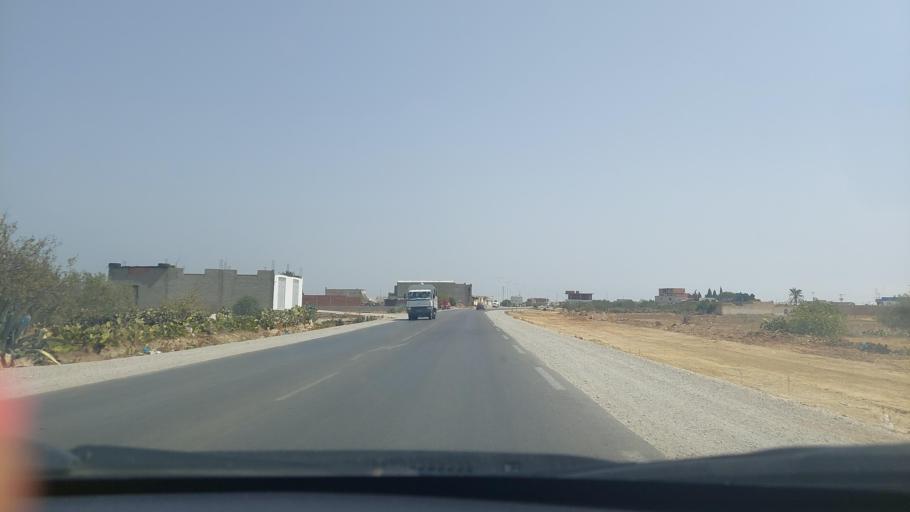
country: TN
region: Al Munastir
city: Qasr Hallal
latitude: 35.6047
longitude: 10.8865
